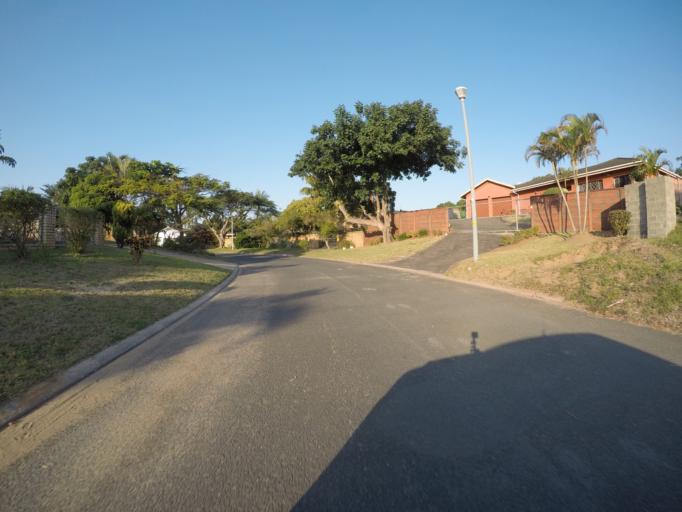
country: ZA
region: KwaZulu-Natal
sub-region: uThungulu District Municipality
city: Richards Bay
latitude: -28.7775
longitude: 32.1138
